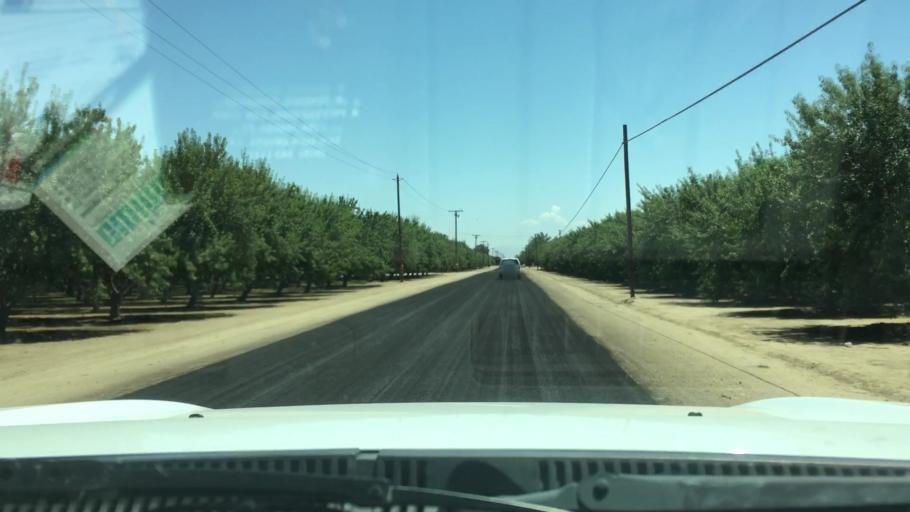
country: US
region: California
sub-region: Kern County
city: Shafter
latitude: 35.5290
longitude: -119.3251
